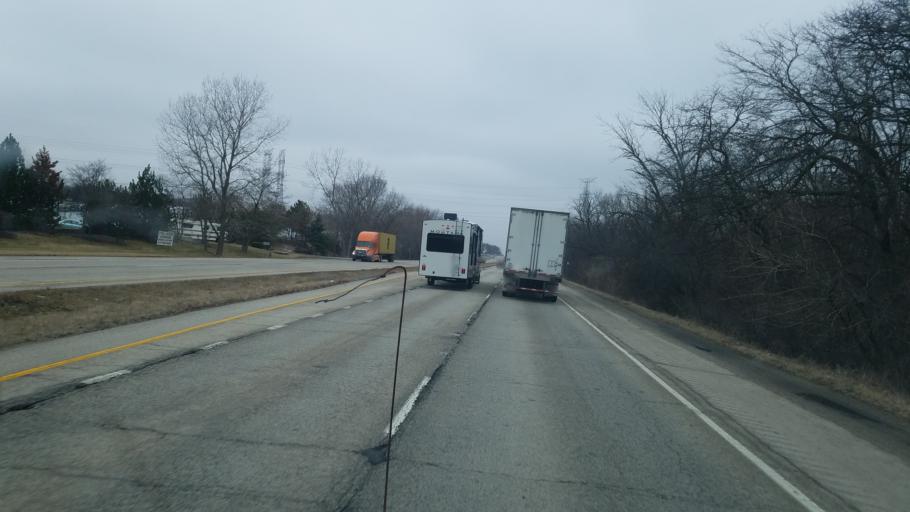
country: US
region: Illinois
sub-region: Lake County
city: Gurnee
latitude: 42.3818
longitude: -87.9179
